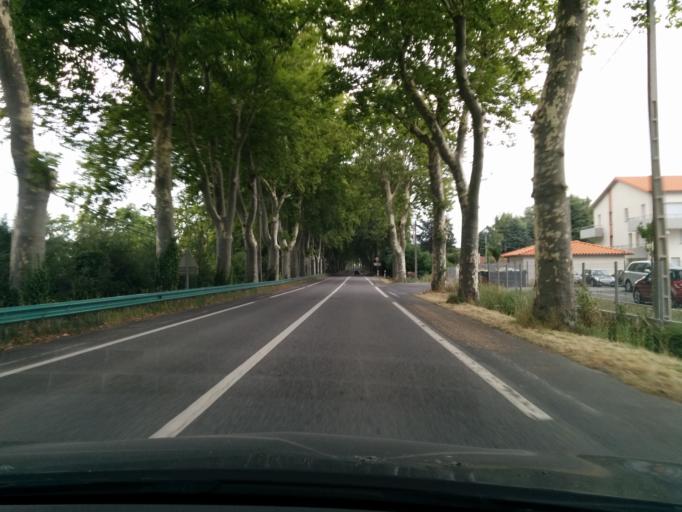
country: FR
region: Midi-Pyrenees
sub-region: Departement de la Haute-Garonne
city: Villefranche-de-Lauragais
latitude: 43.4079
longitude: 1.7071
